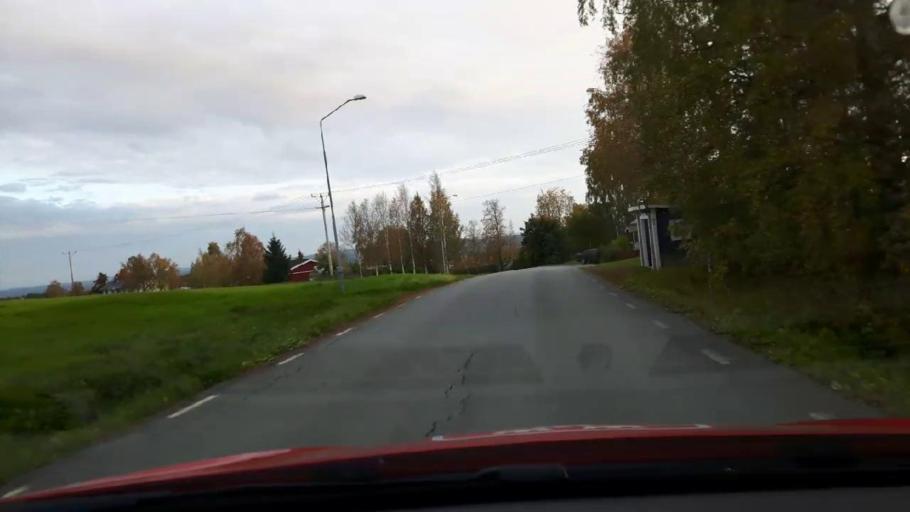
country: SE
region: Jaemtland
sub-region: Krokoms Kommun
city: Krokom
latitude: 63.3651
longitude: 14.4788
